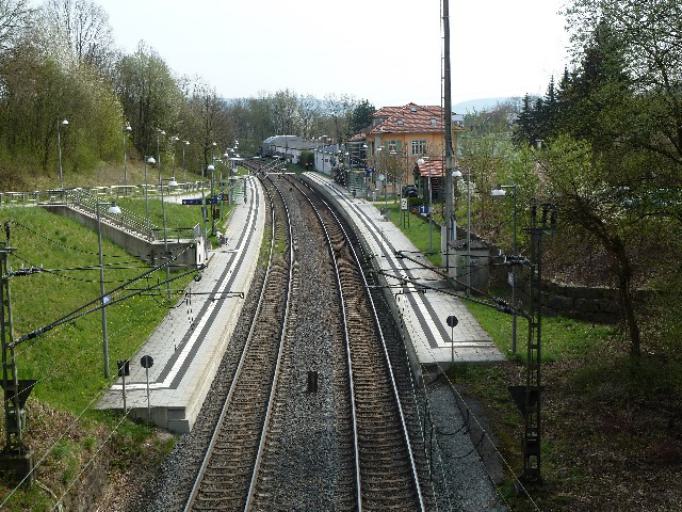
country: DE
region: Baden-Wuerttemberg
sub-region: Karlsruhe Region
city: Obrigheim
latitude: 49.3731
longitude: 9.0830
